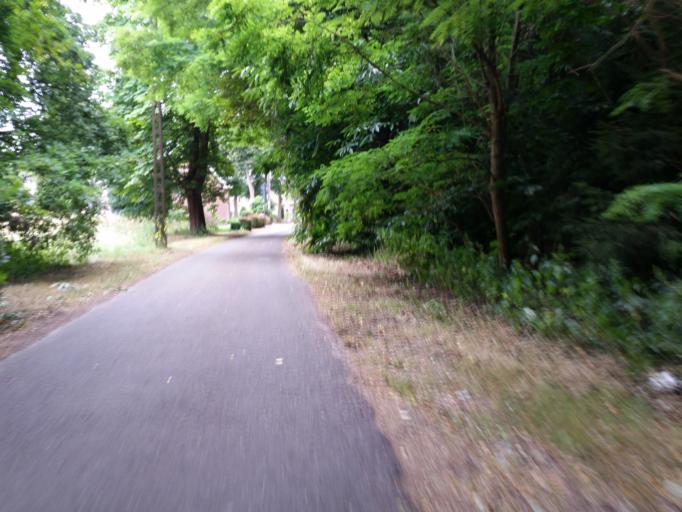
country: BE
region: Flanders
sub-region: Provincie Antwerpen
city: Rumst
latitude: 51.0600
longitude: 4.4529
